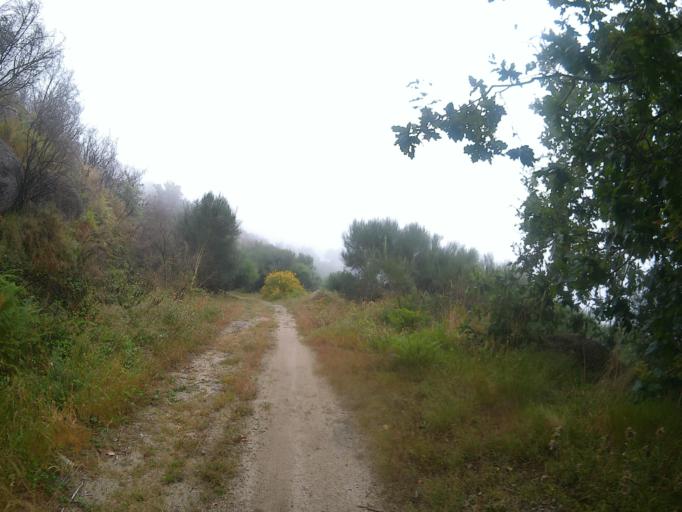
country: PT
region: Viana do Castelo
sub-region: Ponte de Lima
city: Ponte de Lima
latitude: 41.7100
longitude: -8.6060
